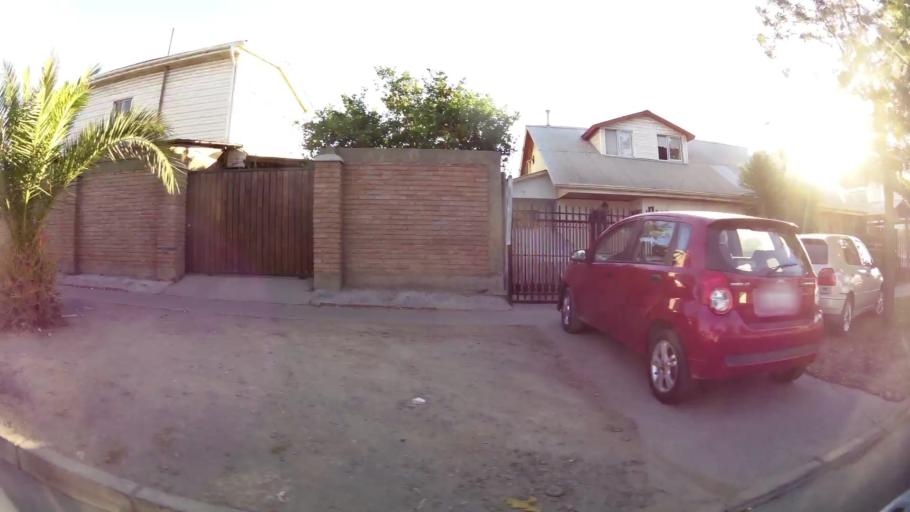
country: CL
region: O'Higgins
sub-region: Provincia de Cachapoal
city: Rancagua
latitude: -34.1733
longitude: -70.7643
